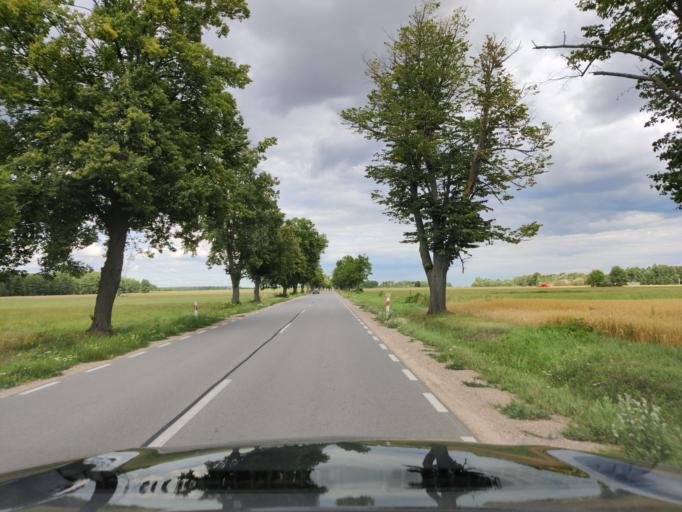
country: PL
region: Masovian Voivodeship
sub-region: Powiat sokolowski
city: Kosow Lacki
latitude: 52.6050
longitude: 22.1837
